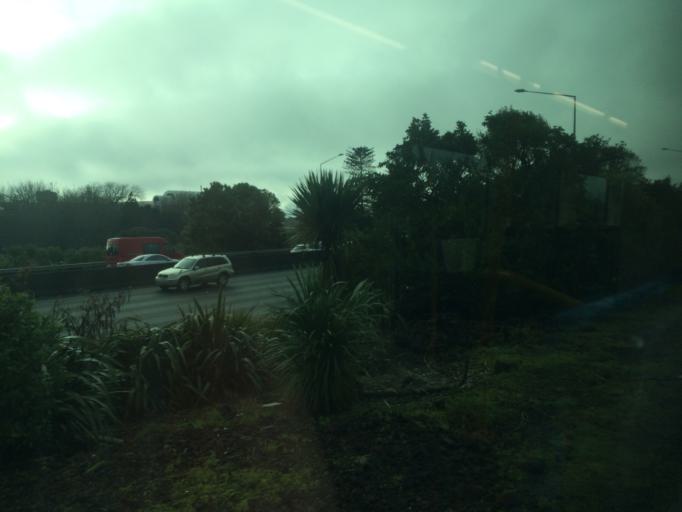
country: NZ
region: Auckland
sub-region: Auckland
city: Auckland
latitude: -36.8910
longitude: 174.7999
